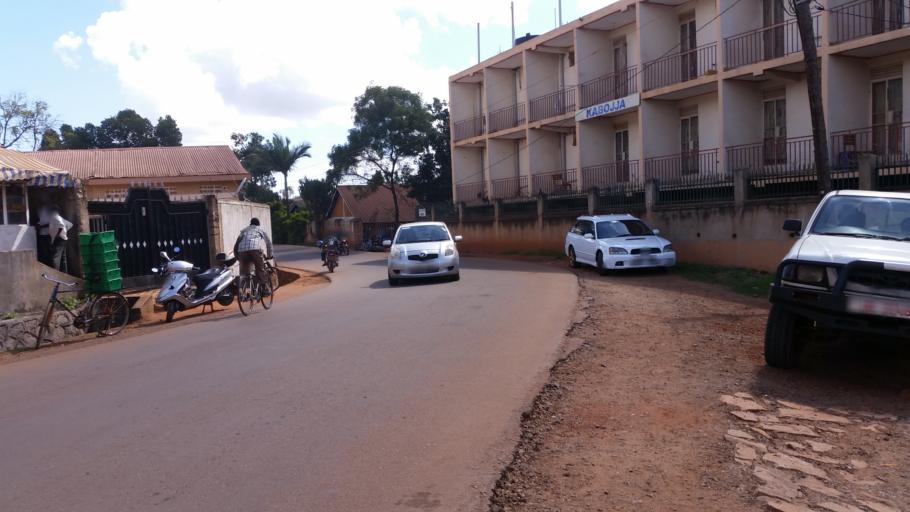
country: UG
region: Central Region
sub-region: Wakiso District
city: Kireka
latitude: 0.3561
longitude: 32.6368
